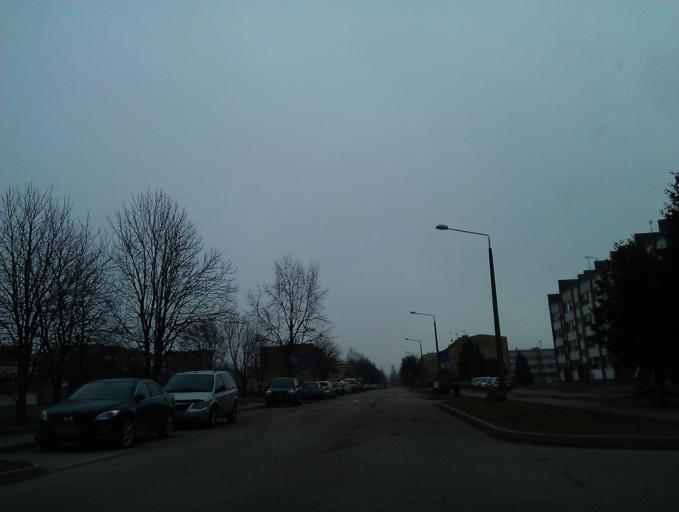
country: LV
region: Adazi
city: Adazi
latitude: 57.0811
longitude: 24.3210
